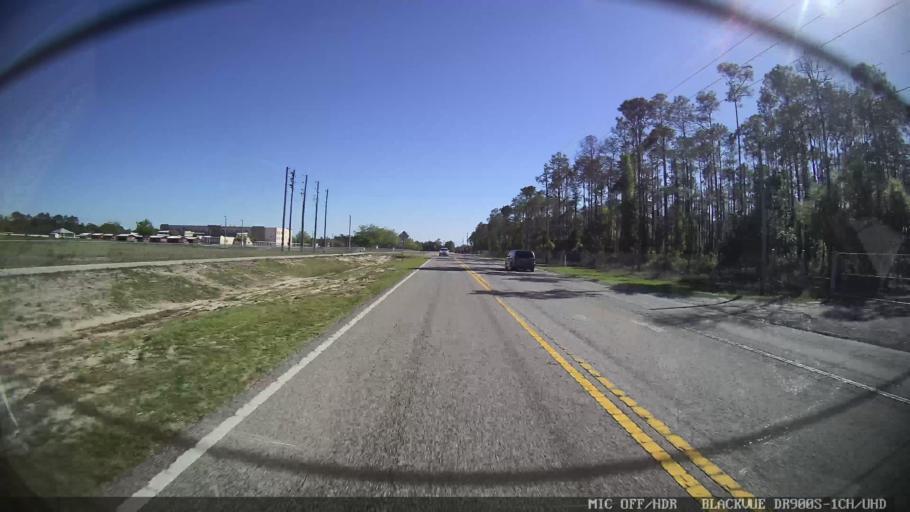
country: US
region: Florida
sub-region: Pasco County
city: Shady Hills
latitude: 28.3793
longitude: -82.5511
